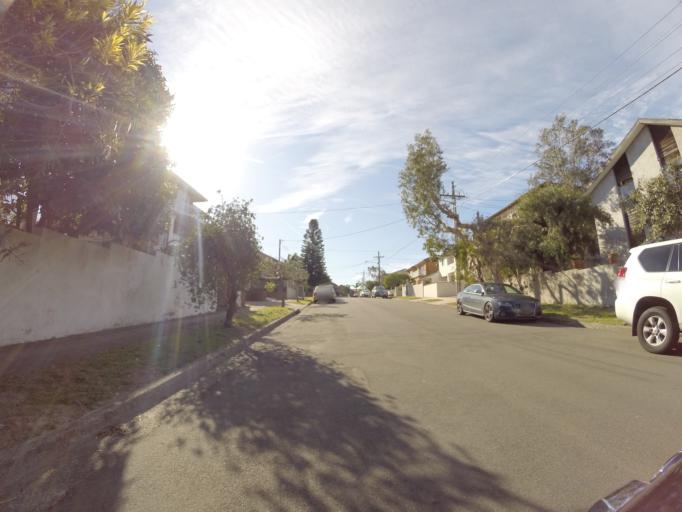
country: AU
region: New South Wales
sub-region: Randwick
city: South Coogee
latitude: -33.9393
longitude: 151.2547
